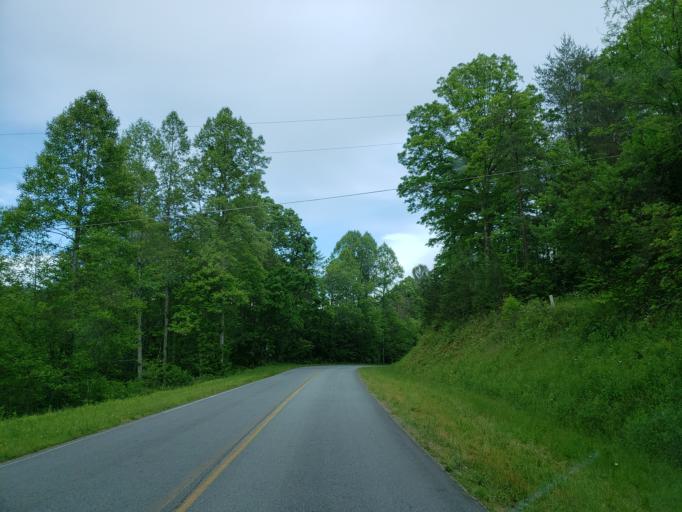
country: US
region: Georgia
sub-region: Fannin County
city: Blue Ridge
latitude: 34.8689
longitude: -84.3596
